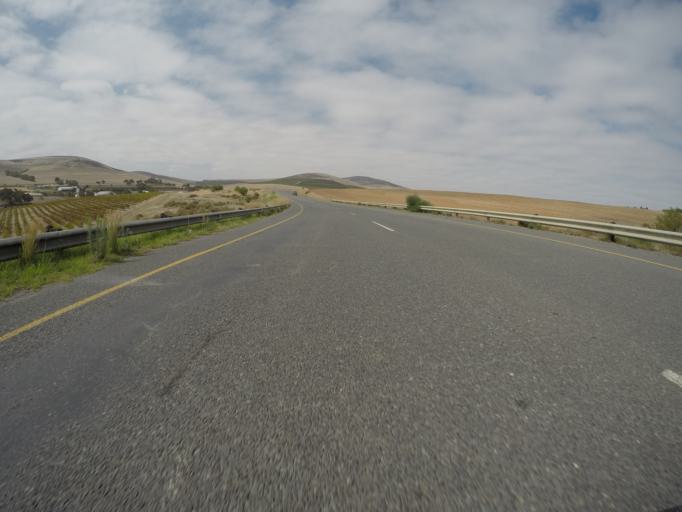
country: ZA
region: Western Cape
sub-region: City of Cape Town
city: Sunset Beach
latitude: -33.7885
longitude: 18.5774
